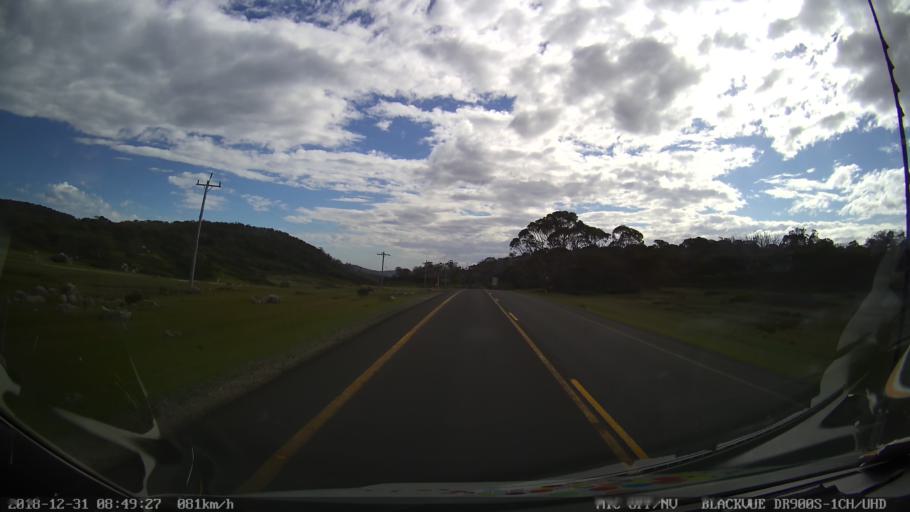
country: AU
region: New South Wales
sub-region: Snowy River
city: Jindabyne
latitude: -36.3616
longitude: 148.5073
